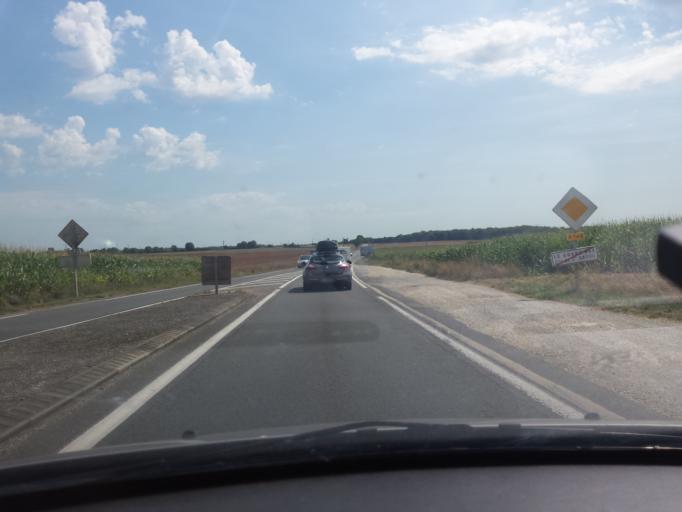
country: FR
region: Poitou-Charentes
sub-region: Departement de la Vienne
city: Civray
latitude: 46.1438
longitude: 0.2273
